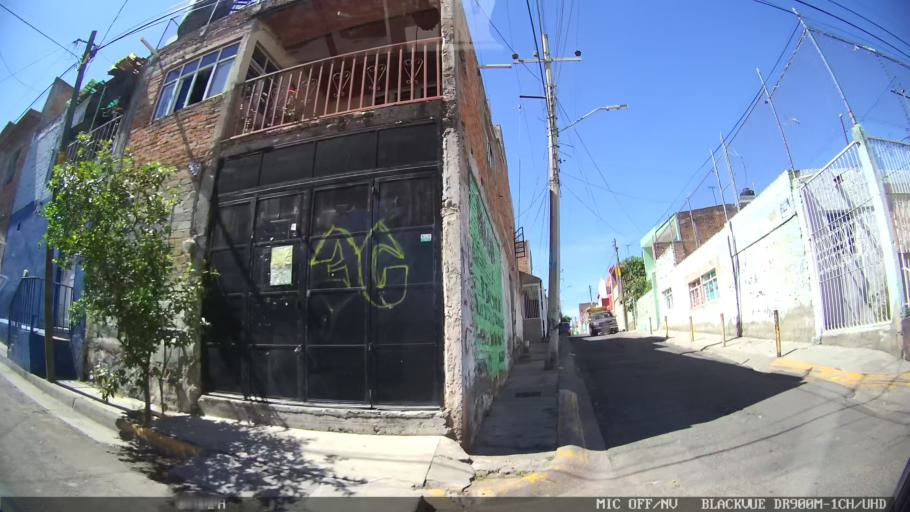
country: MX
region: Jalisco
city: Tlaquepaque
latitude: 20.6970
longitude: -103.2806
